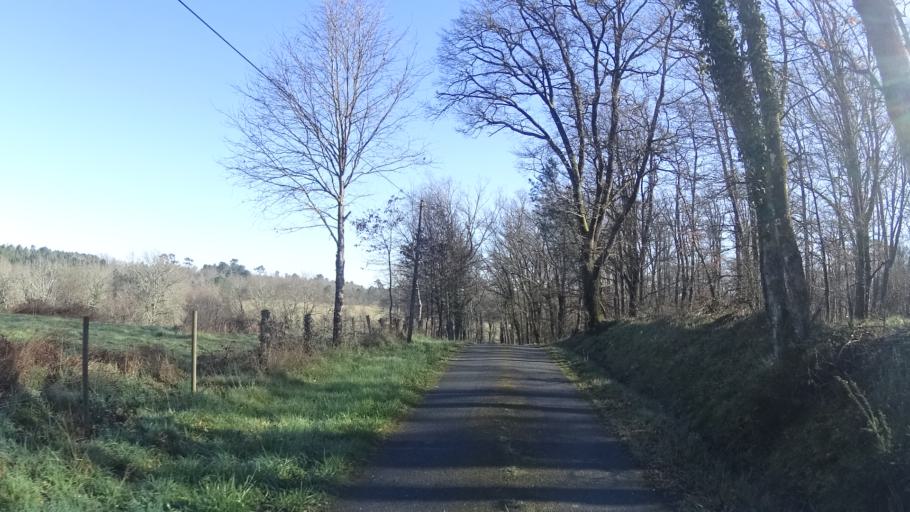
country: FR
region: Aquitaine
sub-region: Departement de la Dordogne
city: La Roche-Chalais
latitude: 45.1576
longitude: 0.0171
